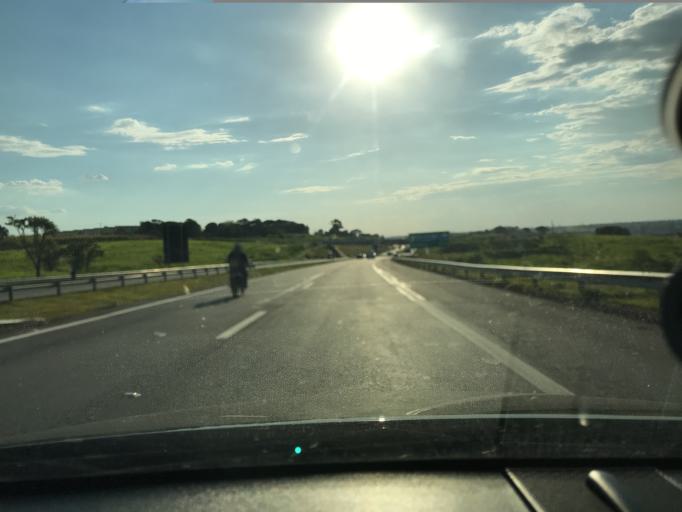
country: BR
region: Sao Paulo
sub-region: Valinhos
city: Valinhos
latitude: -22.9880
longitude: -47.0573
